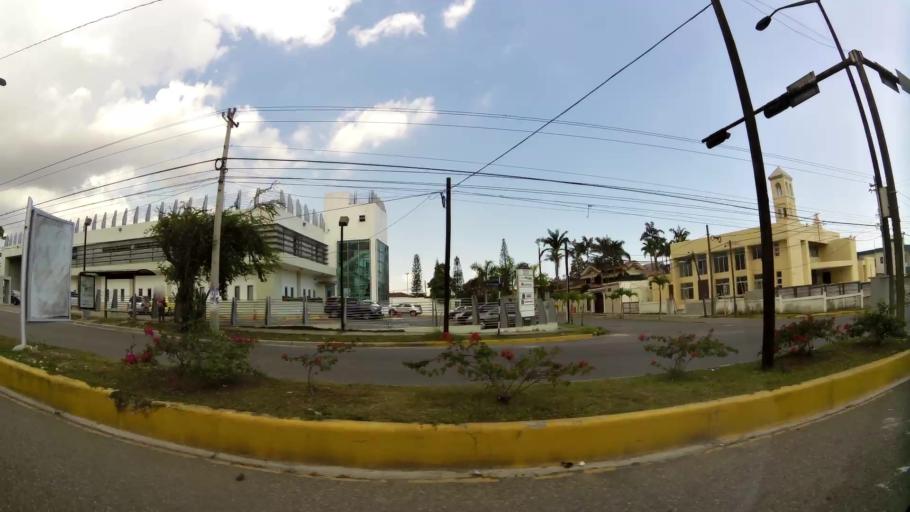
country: DO
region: Santo Domingo
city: Santo Domingo Oeste
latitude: 18.4922
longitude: -70.0000
